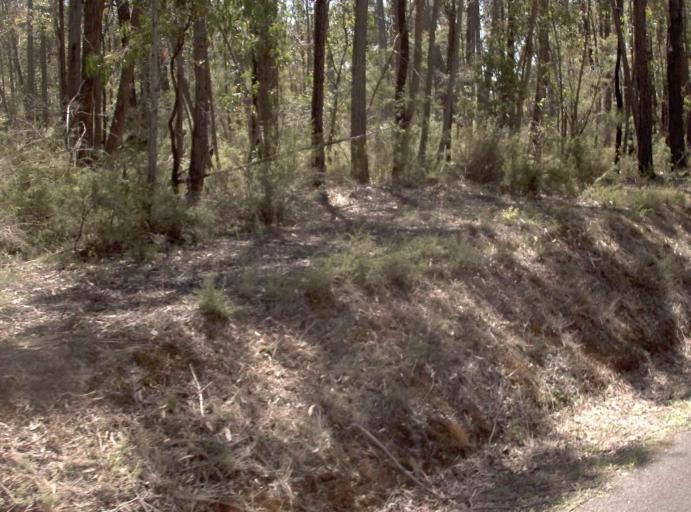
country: AU
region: Victoria
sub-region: East Gippsland
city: Lakes Entrance
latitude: -37.7495
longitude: 148.0695
